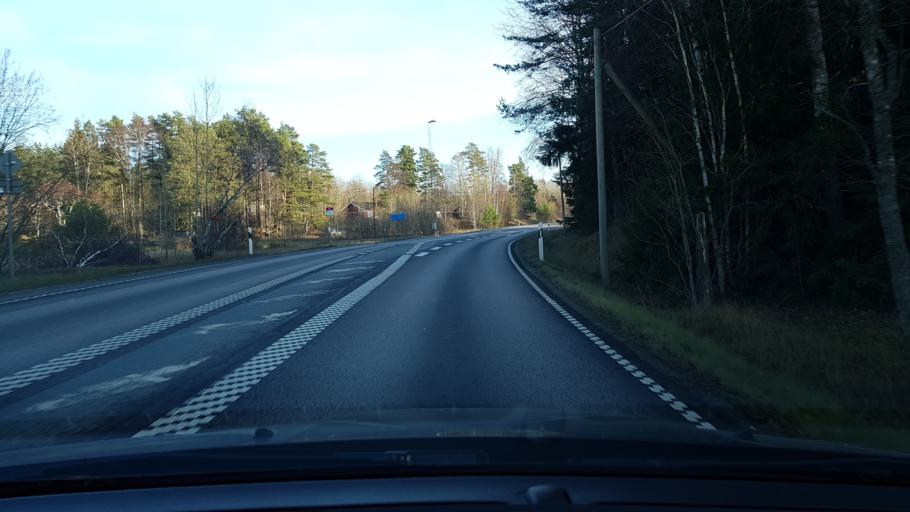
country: SE
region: Stockholm
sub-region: Norrtalje Kommun
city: Nykvarn
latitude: 59.7417
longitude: 18.2036
